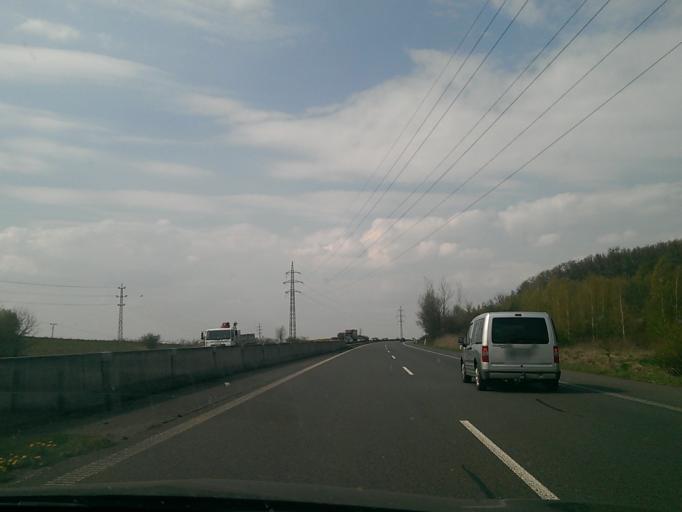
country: CZ
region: Central Bohemia
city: Kosmonosy
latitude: 50.4490
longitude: 14.9382
